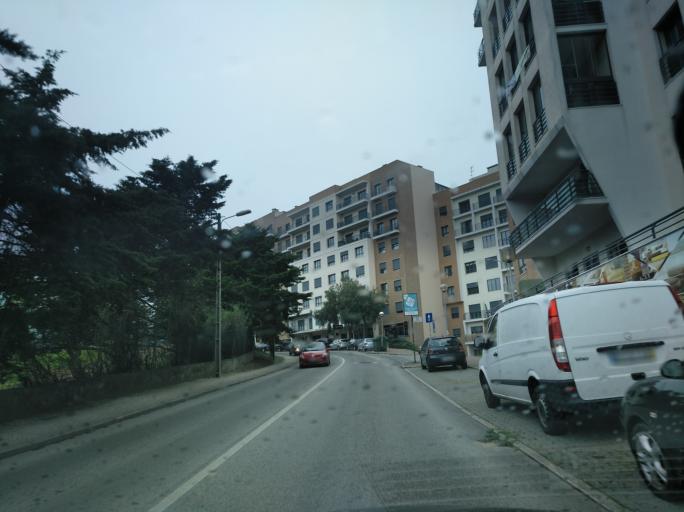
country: PT
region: Lisbon
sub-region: Odivelas
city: Odivelas
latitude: 38.7878
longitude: -9.1936
